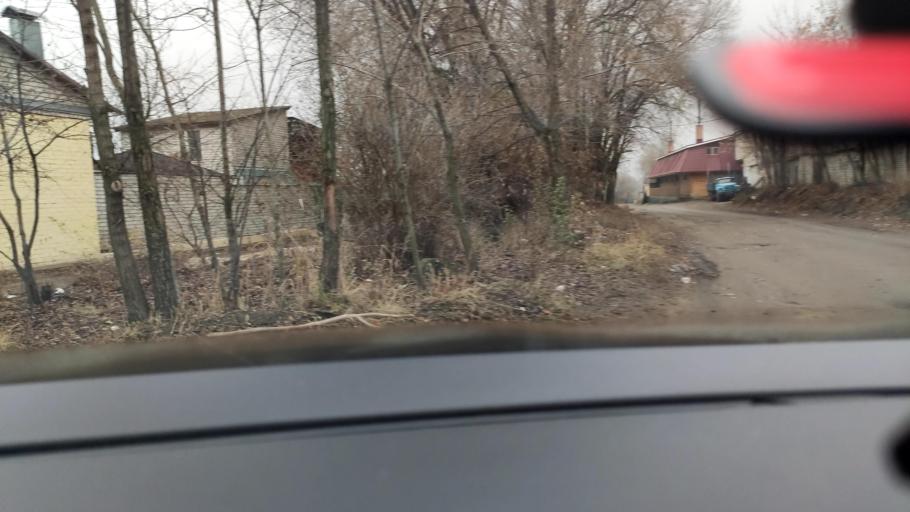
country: RU
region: Voronezj
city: Voronezh
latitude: 51.6366
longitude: 39.1569
